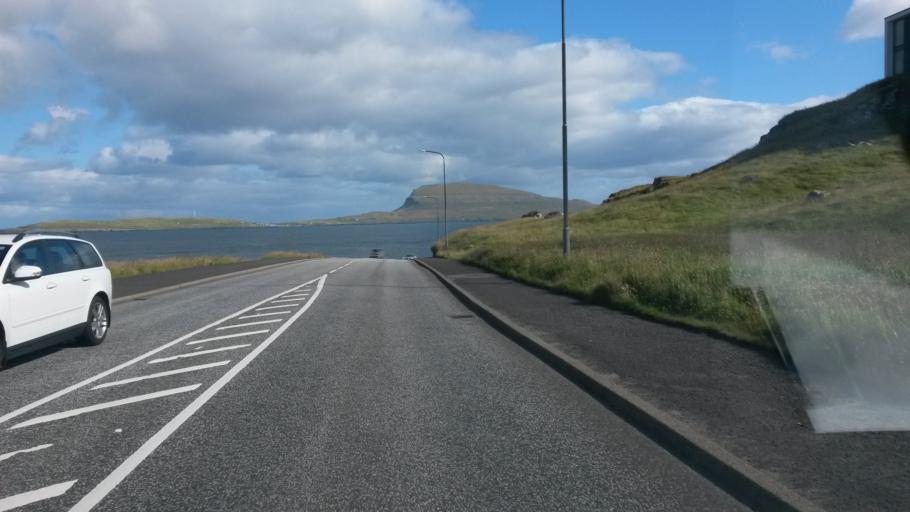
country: FO
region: Streymoy
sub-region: Torshavn
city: Torshavn
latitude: 62.0236
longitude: -6.7619
